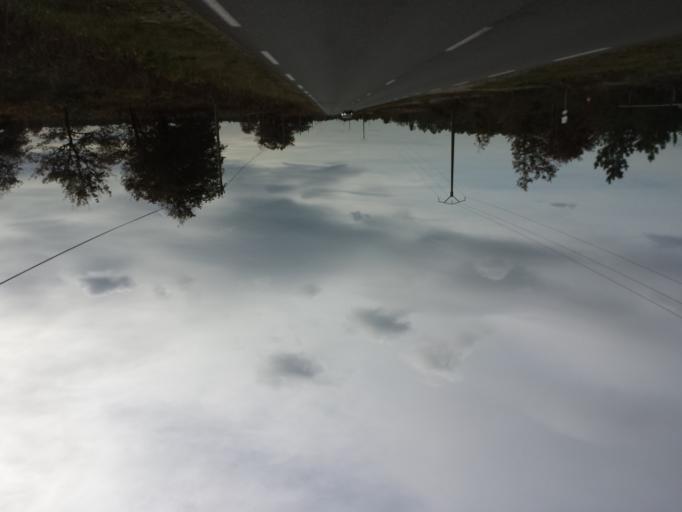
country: FR
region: Aquitaine
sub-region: Departement de la Gironde
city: Marcheprime
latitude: 44.7644
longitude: -0.9229
